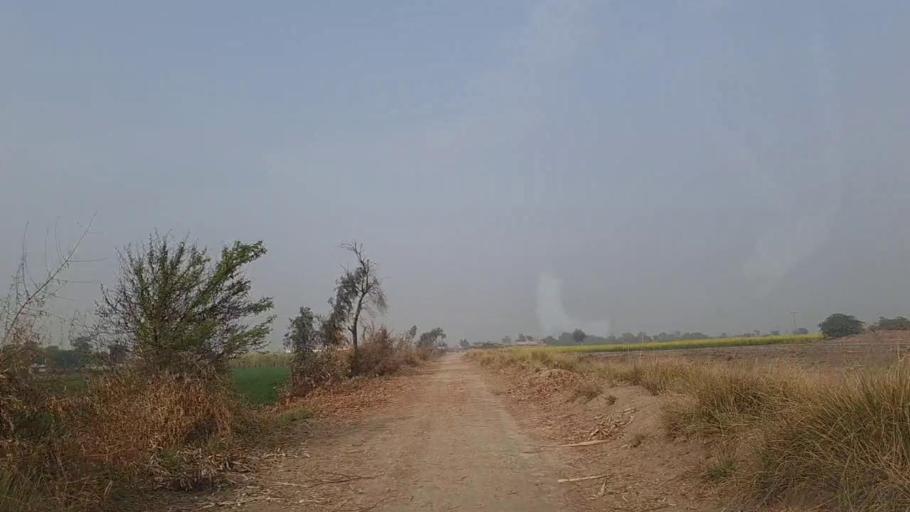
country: PK
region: Sindh
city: Sanghar
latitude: 26.1148
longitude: 68.8963
